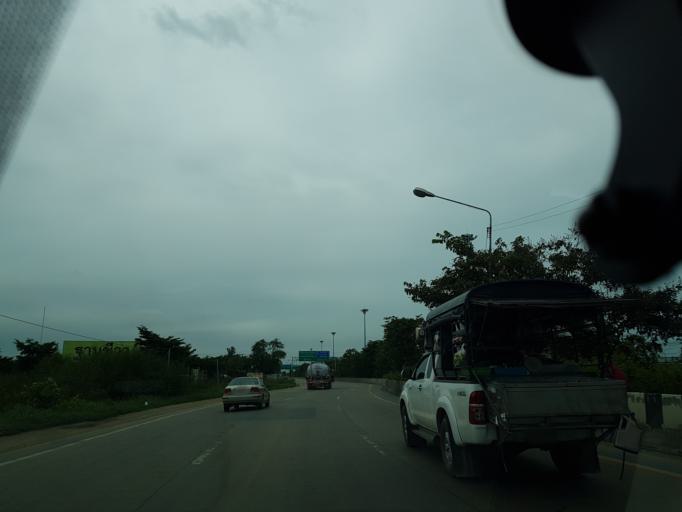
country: TH
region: Phra Nakhon Si Ayutthaya
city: Bang Pa-in
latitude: 14.1678
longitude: 100.5635
